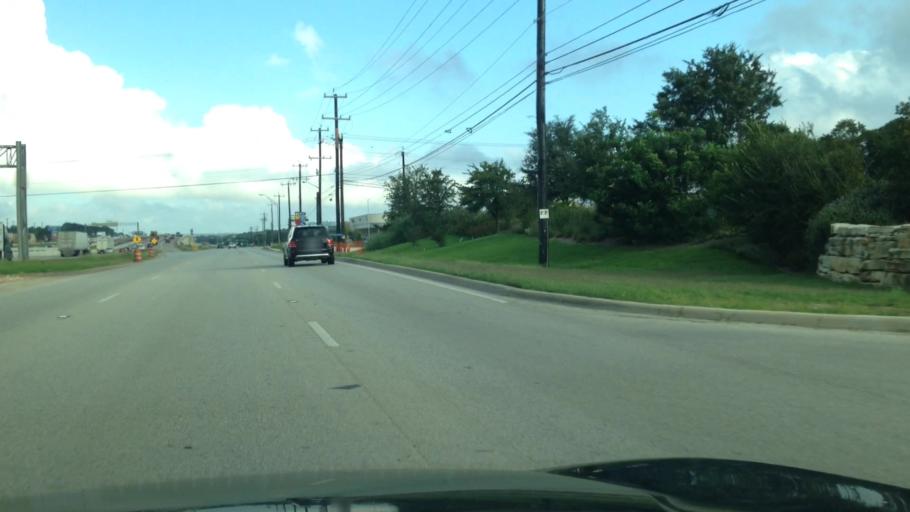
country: US
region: Texas
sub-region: Bexar County
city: Cross Mountain
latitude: 29.6190
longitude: -98.6073
